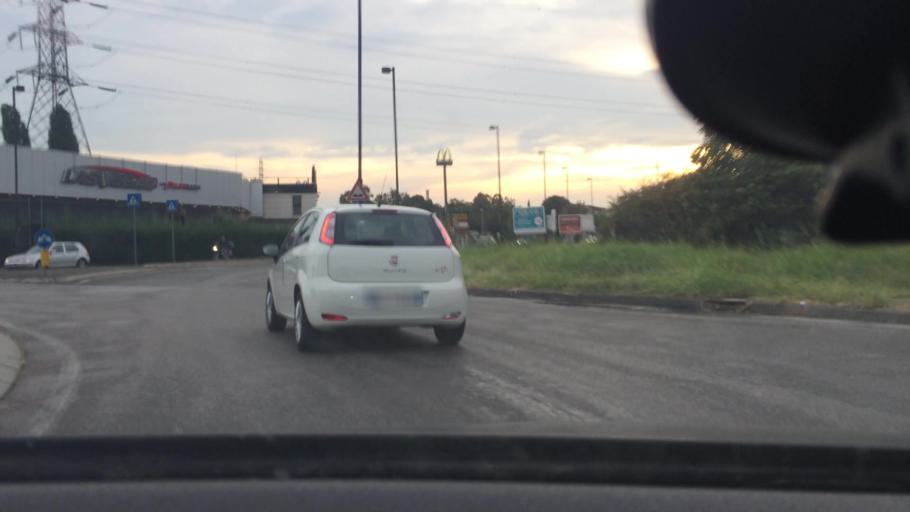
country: IT
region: Lombardy
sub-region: Provincia di Monza e Brianza
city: Varedo
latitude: 45.5963
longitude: 9.1752
